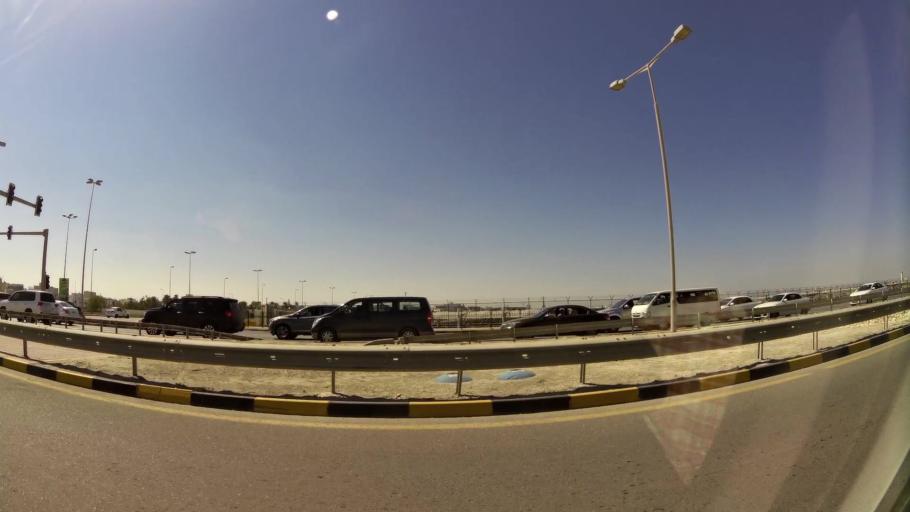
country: BH
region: Muharraq
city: Al Hadd
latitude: 26.2554
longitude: 50.6551
